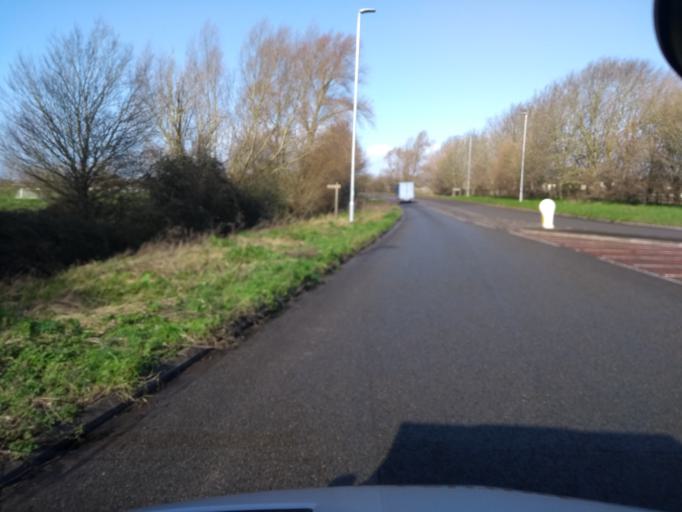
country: GB
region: England
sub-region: Somerset
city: Ilchester
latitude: 50.9982
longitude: -2.6821
